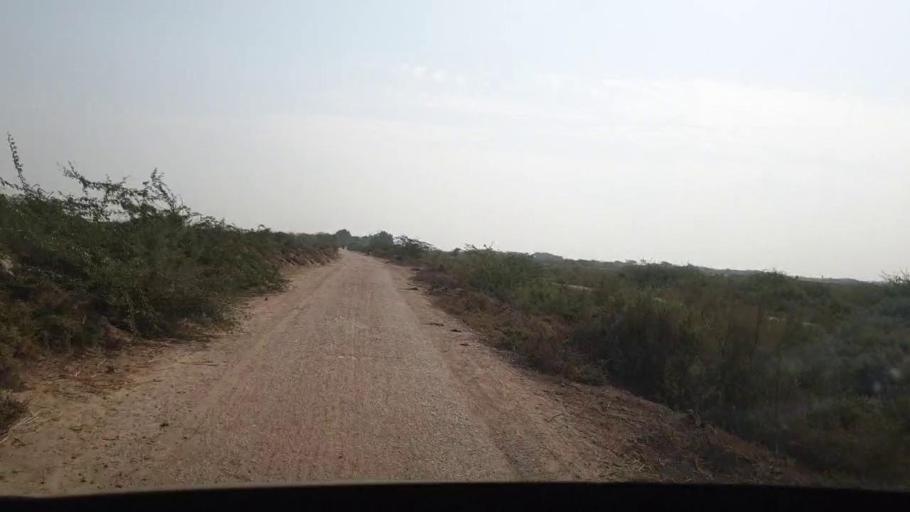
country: PK
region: Sindh
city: Chuhar Jamali
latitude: 24.2470
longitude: 67.9913
